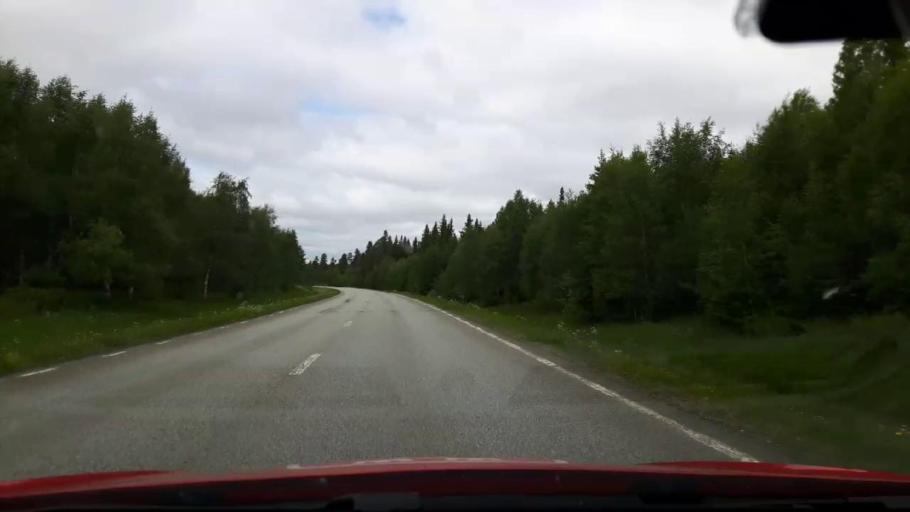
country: SE
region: Jaemtland
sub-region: Krokoms Kommun
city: Krokom
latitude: 63.4310
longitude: 14.4989
